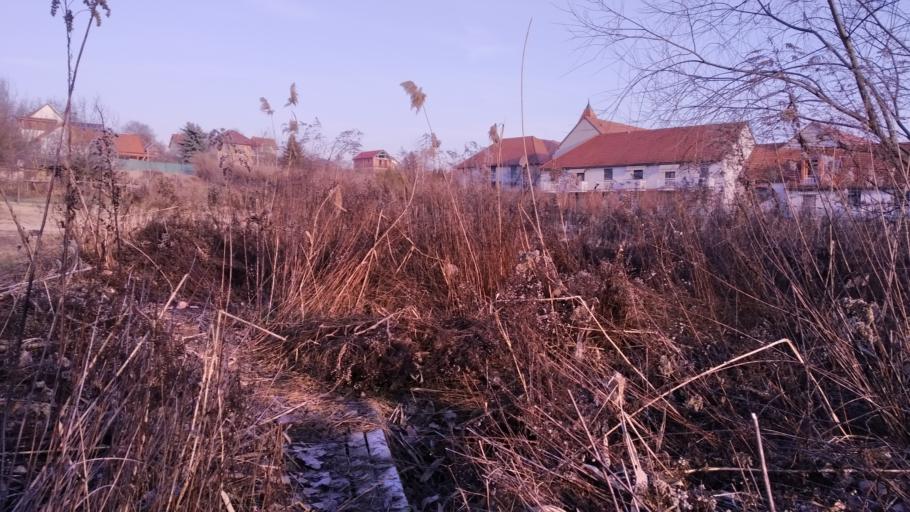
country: HU
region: Pest
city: Budakalasz
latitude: 47.6226
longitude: 19.0361
